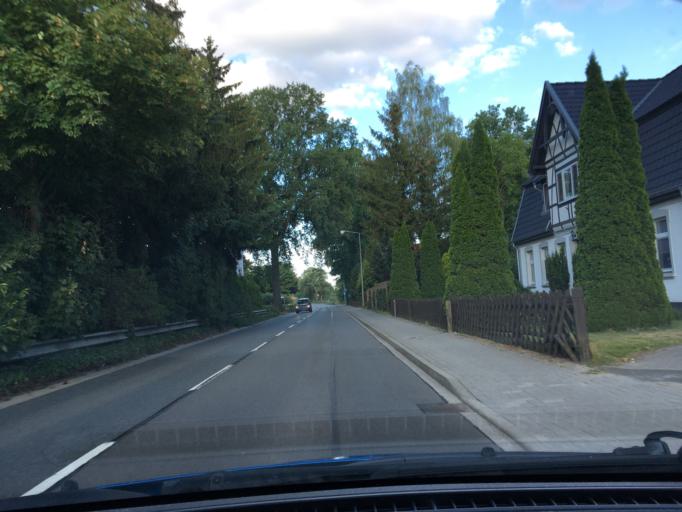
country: DE
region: Lower Saxony
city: Celle
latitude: 52.6050
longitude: 10.1189
